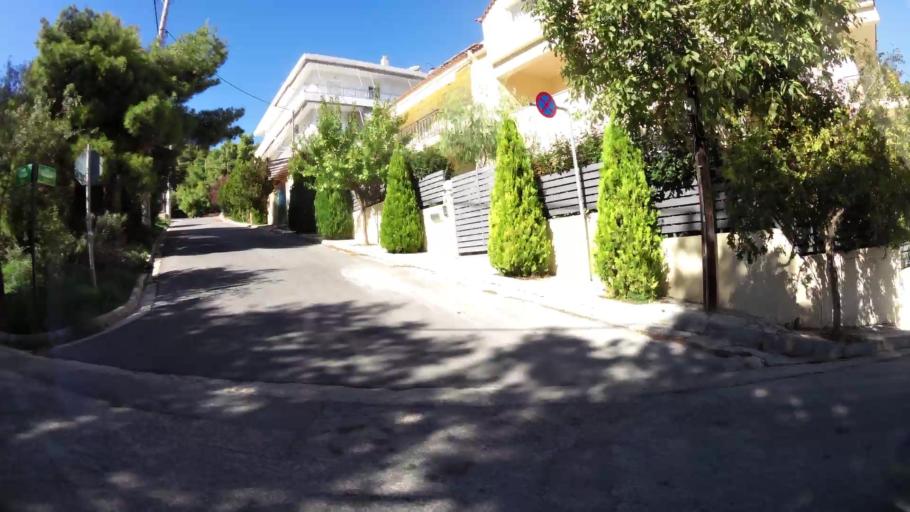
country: GR
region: Attica
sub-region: Nomarchia Anatolikis Attikis
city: Leondarion
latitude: 37.9845
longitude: 23.8609
